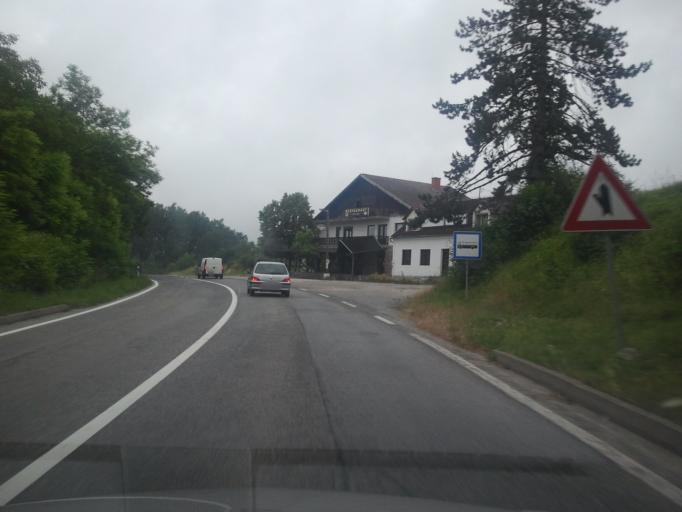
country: HR
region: Karlovacka
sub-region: Grad Karlovac
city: Slunj
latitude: 45.2277
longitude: 15.5574
